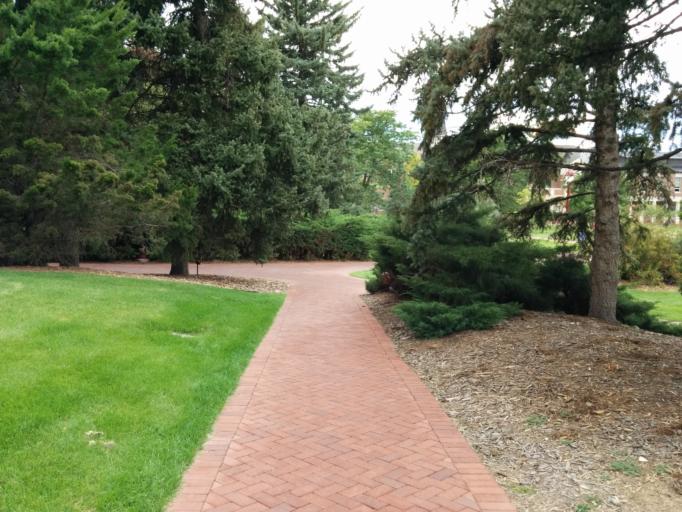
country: US
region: Colorado
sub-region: Arapahoe County
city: Cherry Hills Village
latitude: 39.6769
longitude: -104.9618
